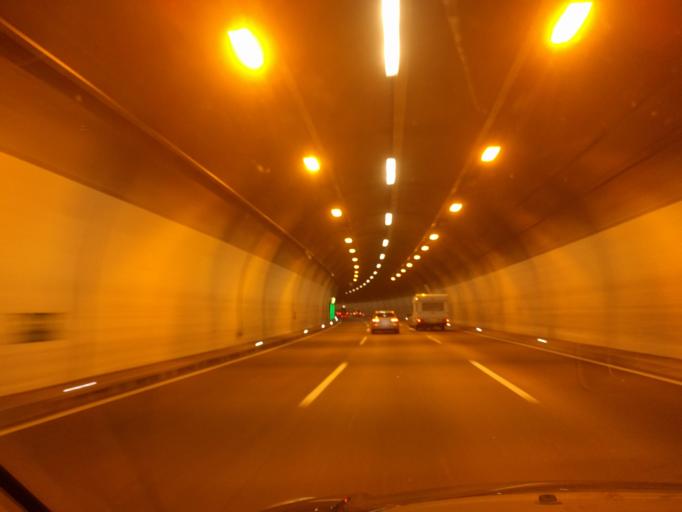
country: CH
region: Ticino
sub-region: Leventina District
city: Faido
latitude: 46.4893
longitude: 8.7577
